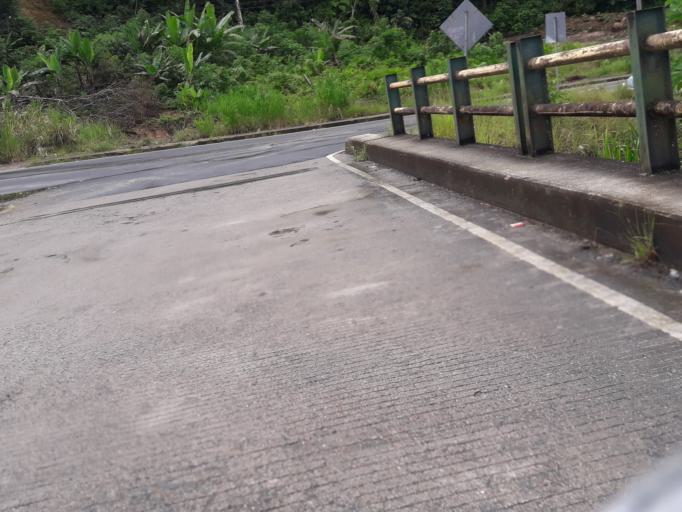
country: EC
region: Napo
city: Tena
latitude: -0.9579
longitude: -77.8600
